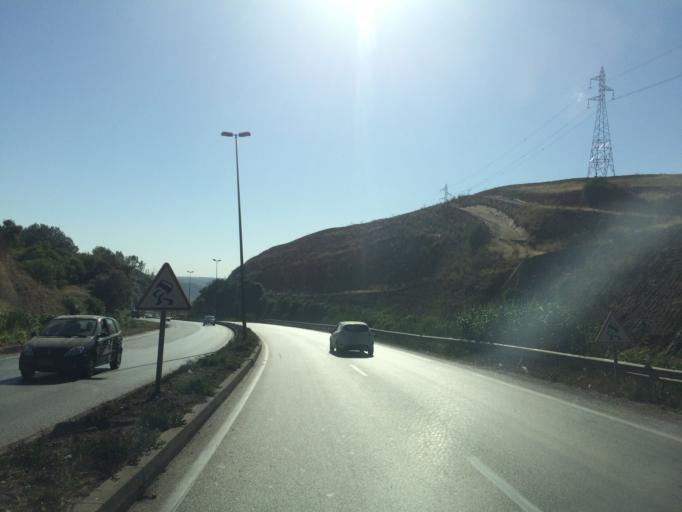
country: MA
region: Rabat-Sale-Zemmour-Zaer
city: Sale
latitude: 33.9851
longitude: -6.7476
